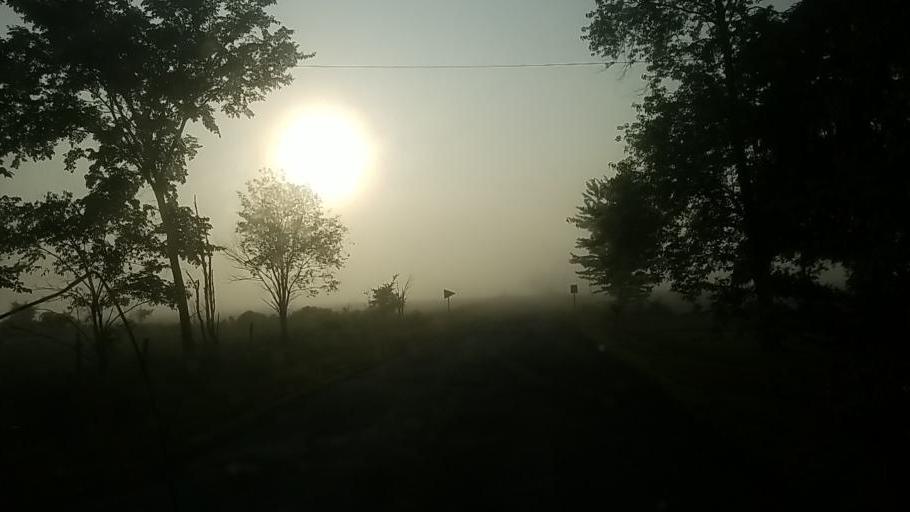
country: US
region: Michigan
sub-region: Muskegon County
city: Twin Lake
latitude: 43.4532
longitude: -86.0717
